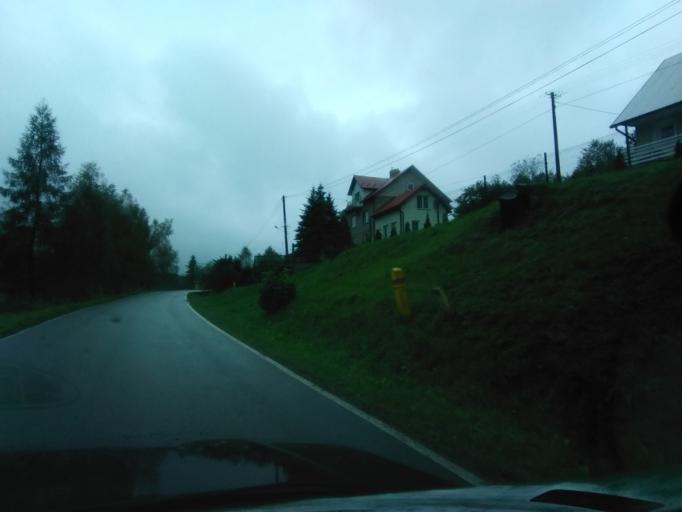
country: PL
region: Subcarpathian Voivodeship
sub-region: Powiat ropczycko-sedziszowski
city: Niedzwiada
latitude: 50.0345
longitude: 21.5461
